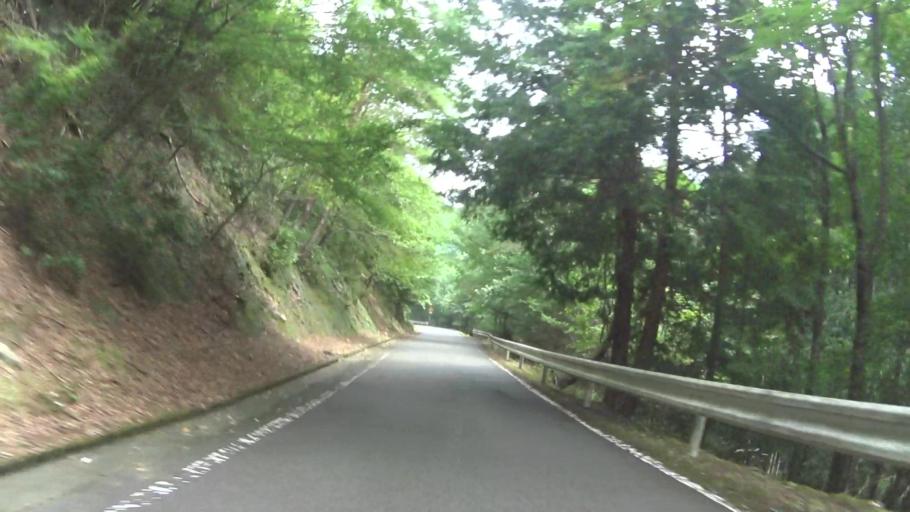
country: JP
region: Kyoto
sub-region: Kyoto-shi
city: Kamigyo-ku
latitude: 35.2043
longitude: 135.6732
